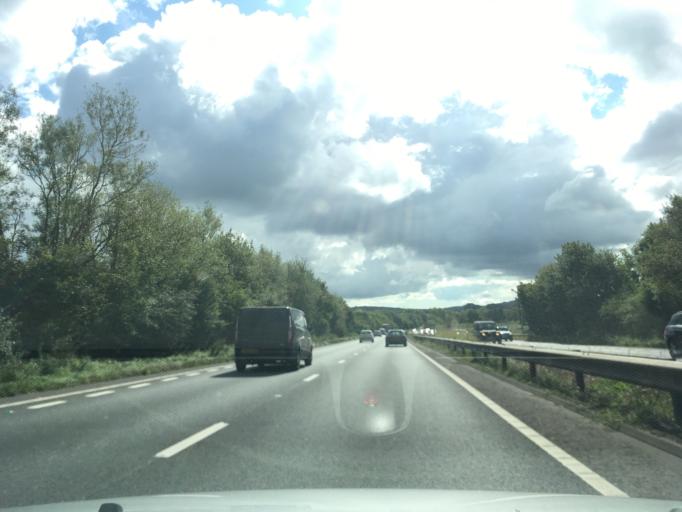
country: GB
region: England
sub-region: Hampshire
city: Petersfield
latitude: 51.0043
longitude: -0.9527
